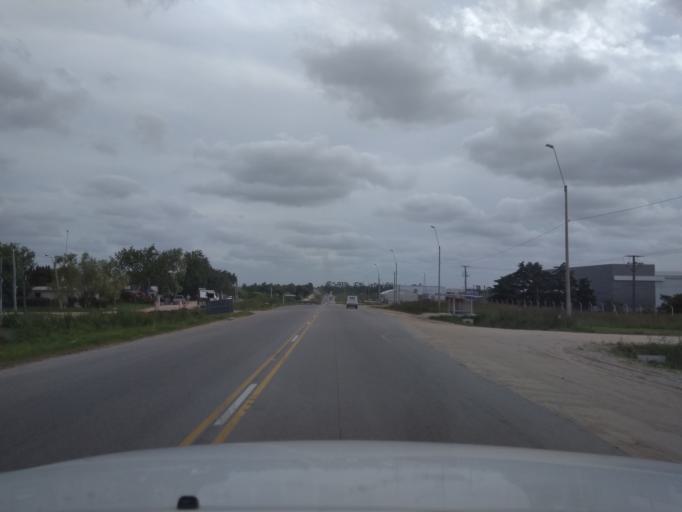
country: UY
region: Canelones
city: Colonia Nicolich
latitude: -34.7888
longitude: -56.0012
